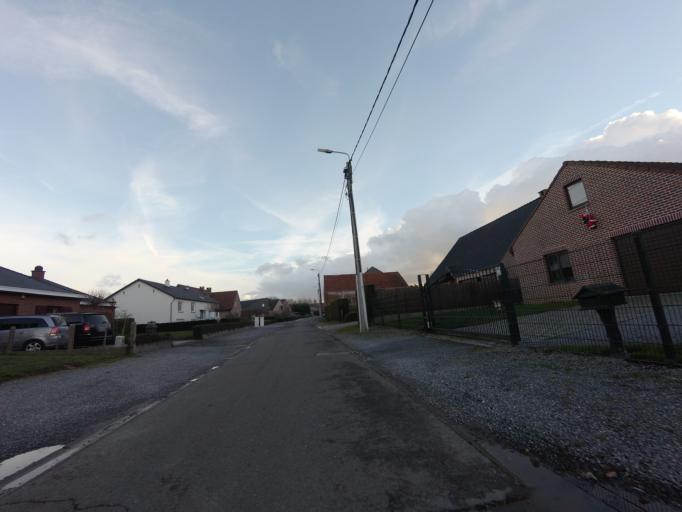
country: BE
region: Flanders
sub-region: Provincie Vlaams-Brabant
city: Kortenberg
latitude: 50.8923
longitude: 4.5868
